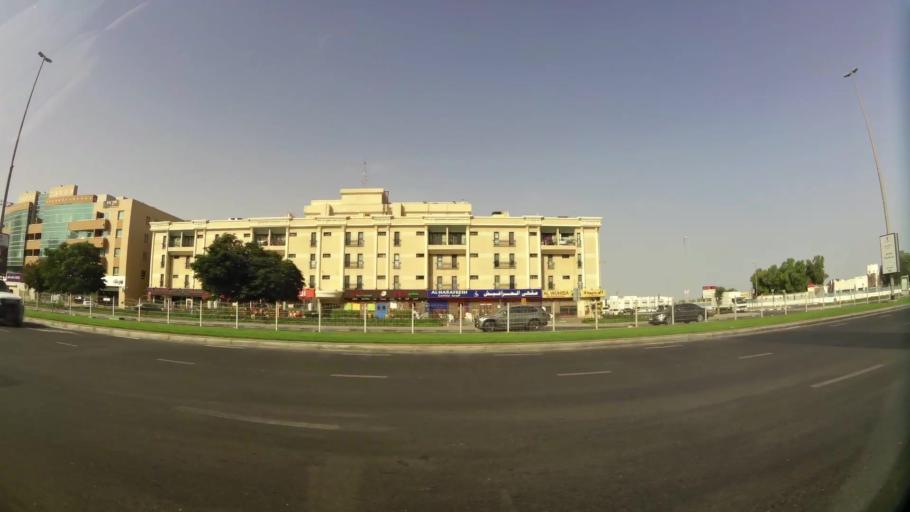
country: AE
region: Ash Shariqah
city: Sharjah
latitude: 25.2846
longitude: 55.3523
